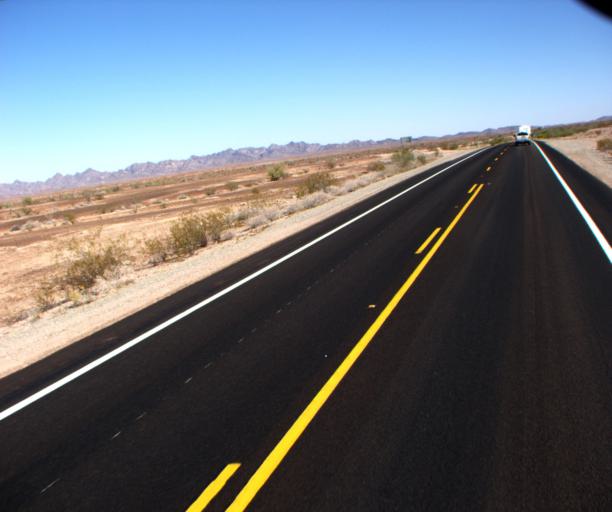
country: US
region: Arizona
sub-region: Yuma County
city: Wellton
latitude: 33.1343
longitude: -114.2879
